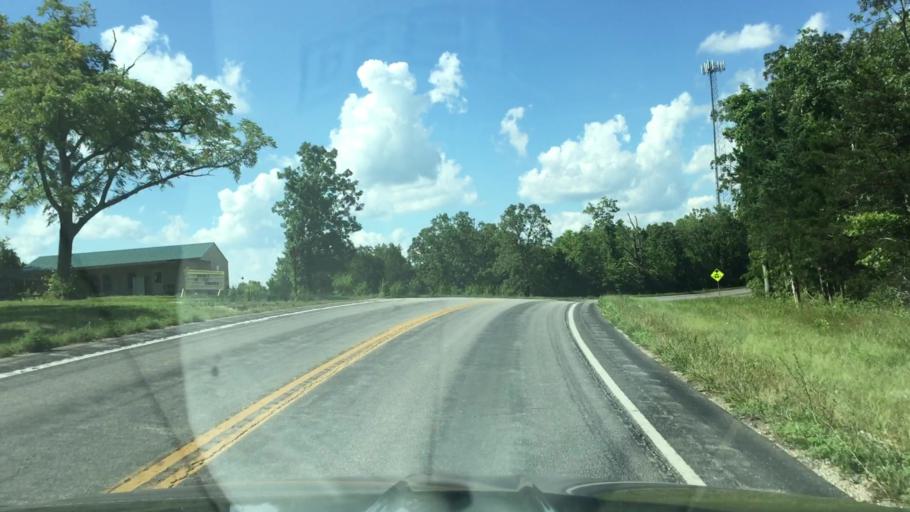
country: US
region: Missouri
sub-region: Miller County
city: Tuscumbia
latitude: 38.0927
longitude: -92.4991
